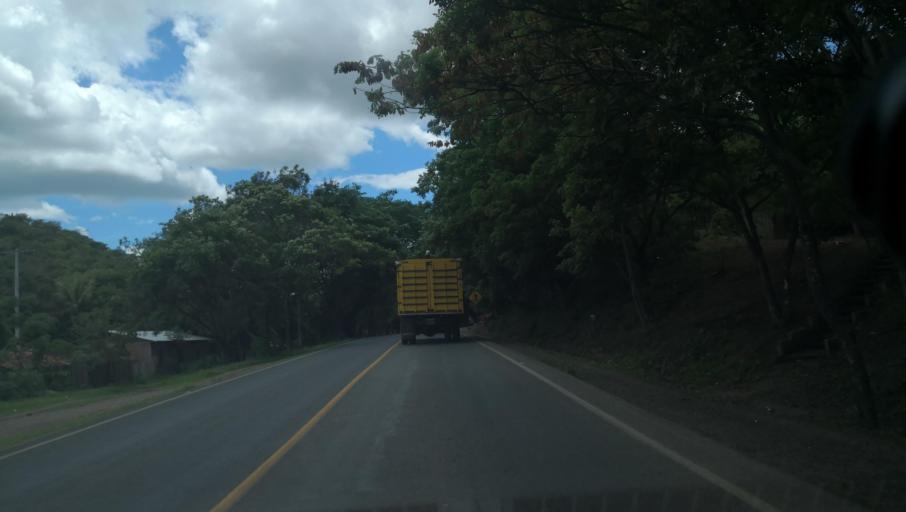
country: NI
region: Madriz
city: Yalaguina
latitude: 13.4747
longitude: -86.4794
